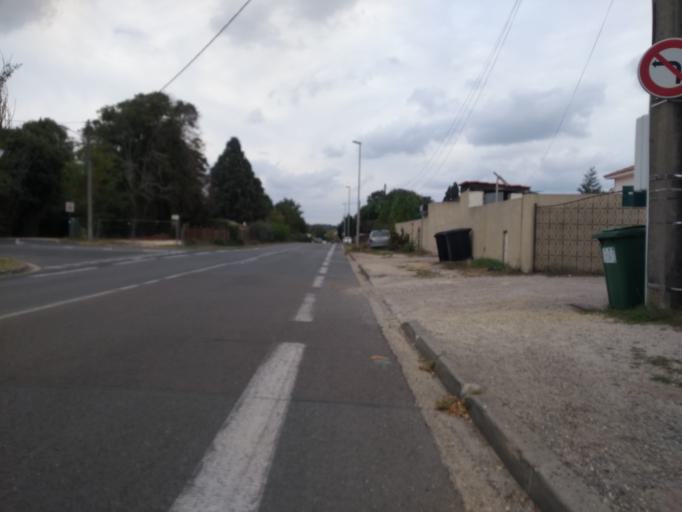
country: FR
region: Aquitaine
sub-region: Departement de la Gironde
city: Pessac
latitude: 44.8214
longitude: -0.6497
